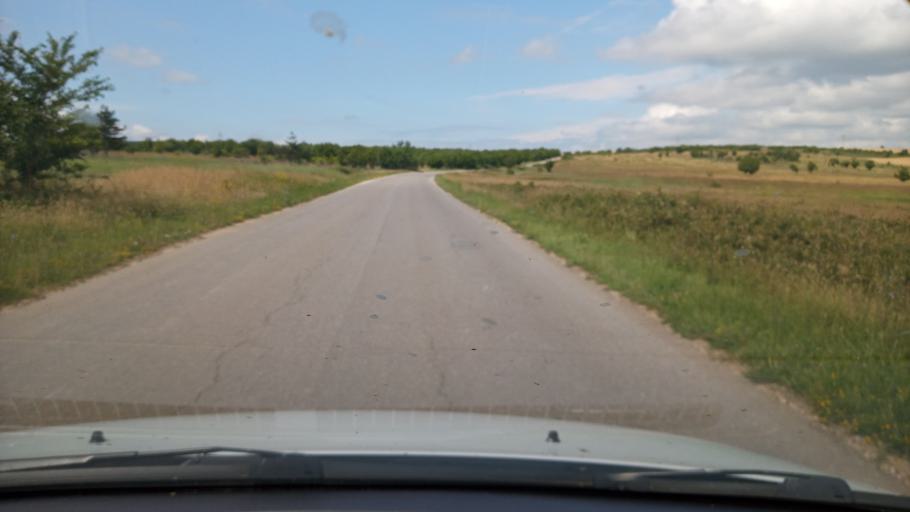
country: BG
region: Lovech
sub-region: Obshtina Lukovit
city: Lukovit
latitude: 43.2038
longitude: 24.1376
